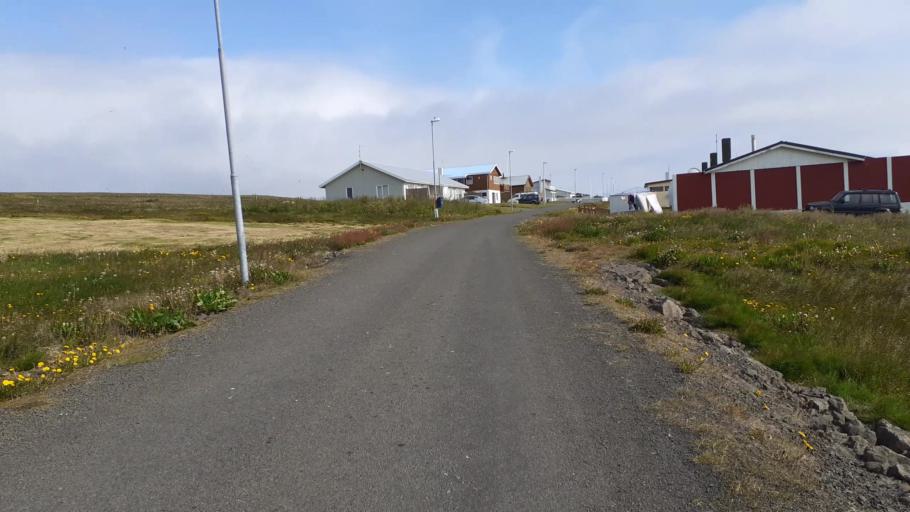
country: IS
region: Northeast
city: Dalvik
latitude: 66.5398
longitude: -18.0140
